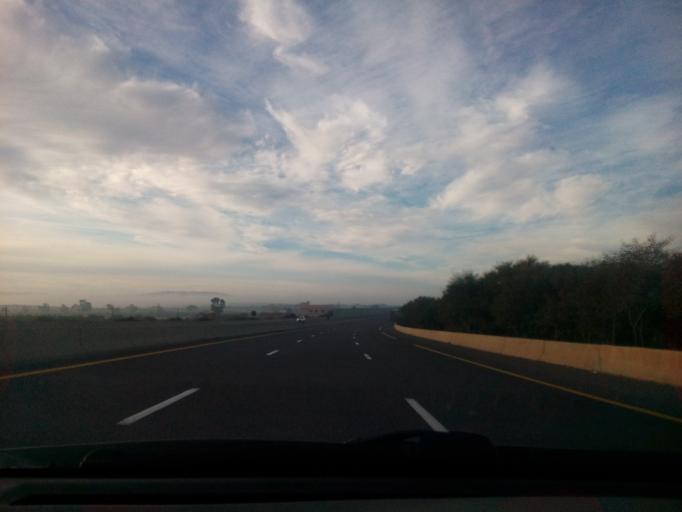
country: DZ
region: Relizane
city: Relizane
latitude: 35.7214
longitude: 0.3001
